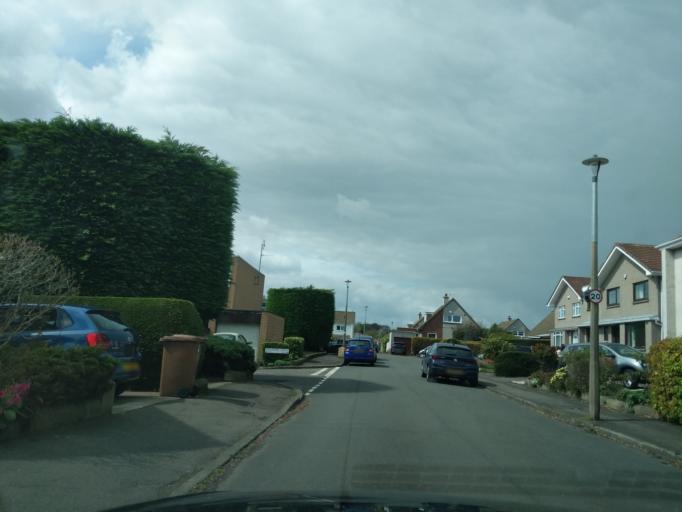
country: GB
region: Scotland
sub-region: Edinburgh
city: Colinton
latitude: 55.9610
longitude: -3.2649
